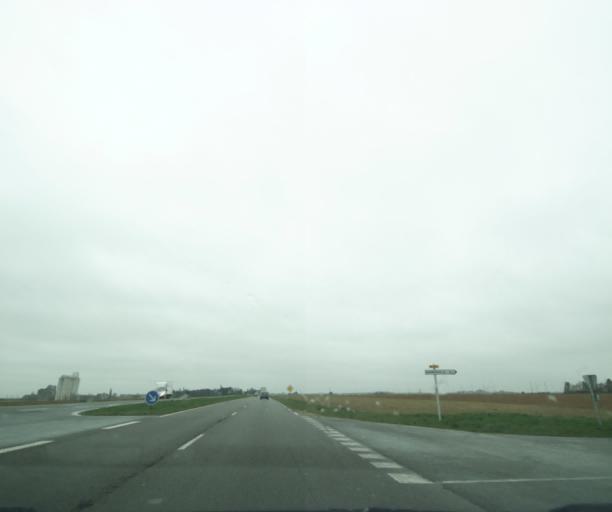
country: FR
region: Ile-de-France
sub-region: Departement de l'Essonne
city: Angerville
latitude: 48.2662
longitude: 1.9715
